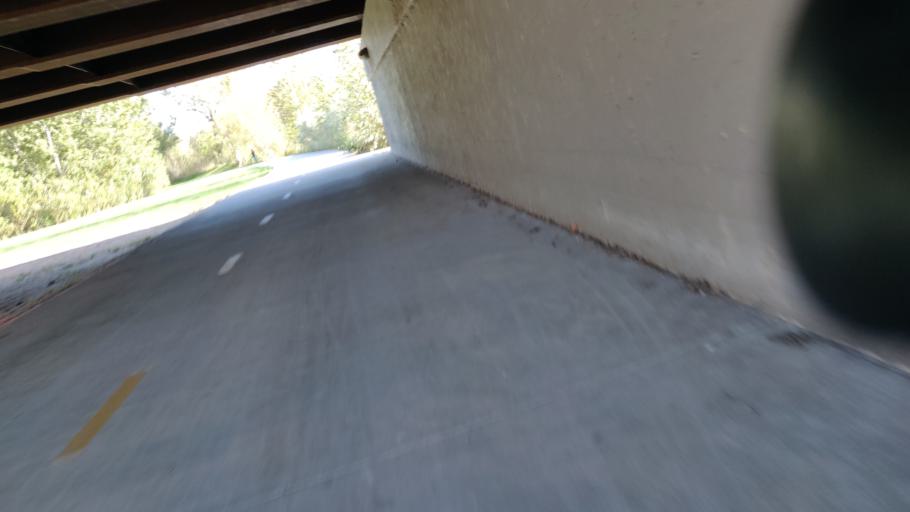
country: US
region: Idaho
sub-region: Ada County
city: Boise
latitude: 43.5763
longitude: -116.1514
